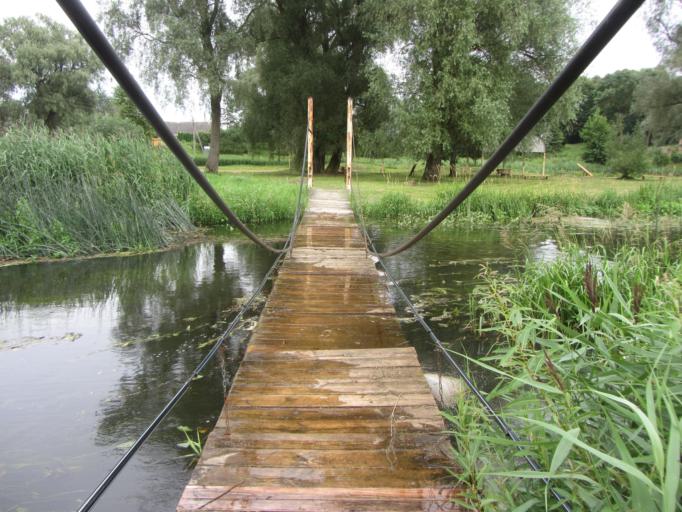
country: LT
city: Kalvarija
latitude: 54.4136
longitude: 23.2080
